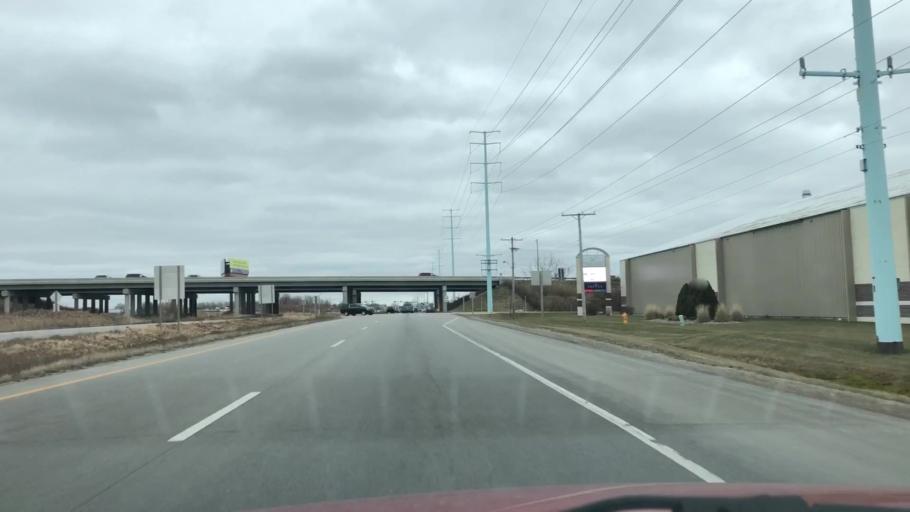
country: US
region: Wisconsin
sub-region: Brown County
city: Ashwaubenon
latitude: 44.4797
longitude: -88.0586
